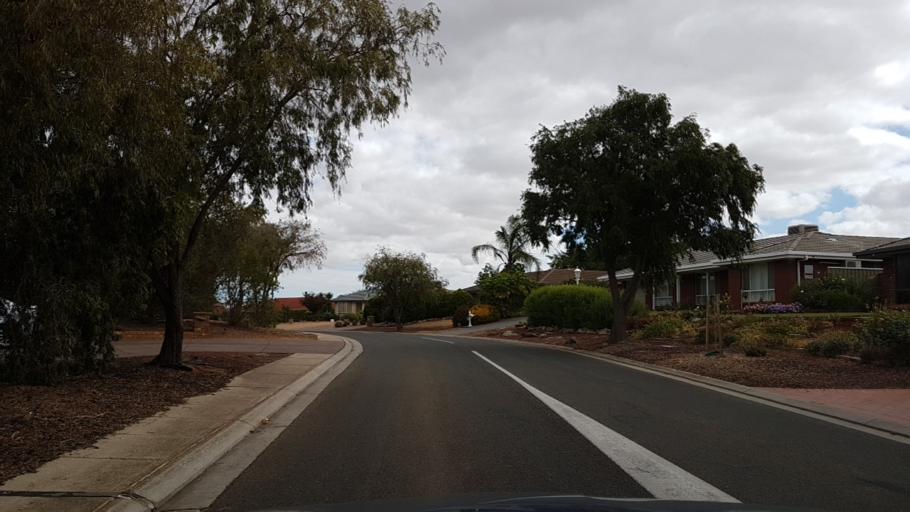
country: AU
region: South Australia
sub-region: Gawler
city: Gawler
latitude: -34.6051
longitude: 138.7628
